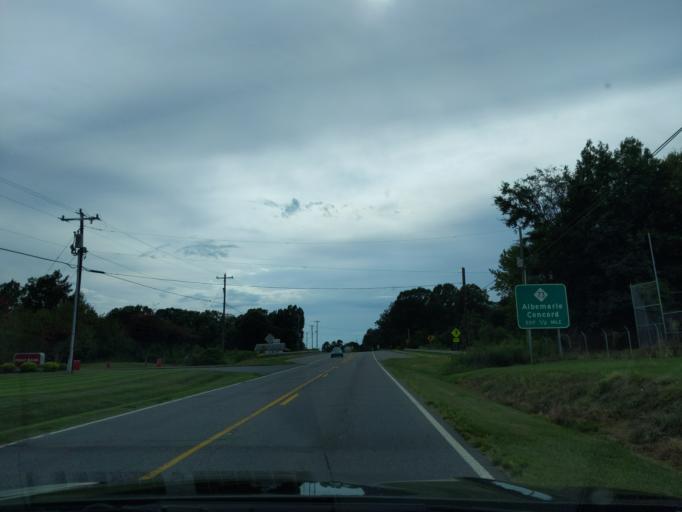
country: US
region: North Carolina
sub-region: Cabarrus County
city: Mount Pleasant
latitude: 35.4107
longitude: -80.4383
